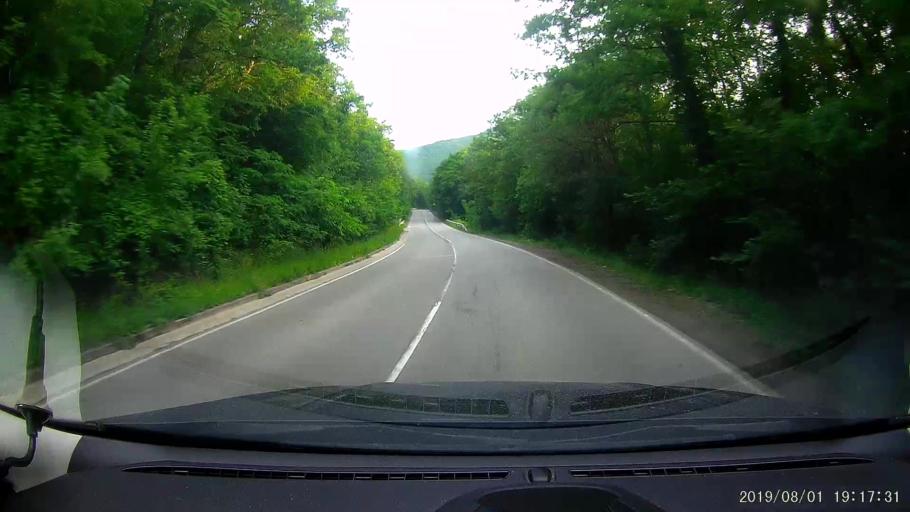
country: BG
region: Shumen
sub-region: Obshtina Smyadovo
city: Smyadovo
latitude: 42.9225
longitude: 26.9418
